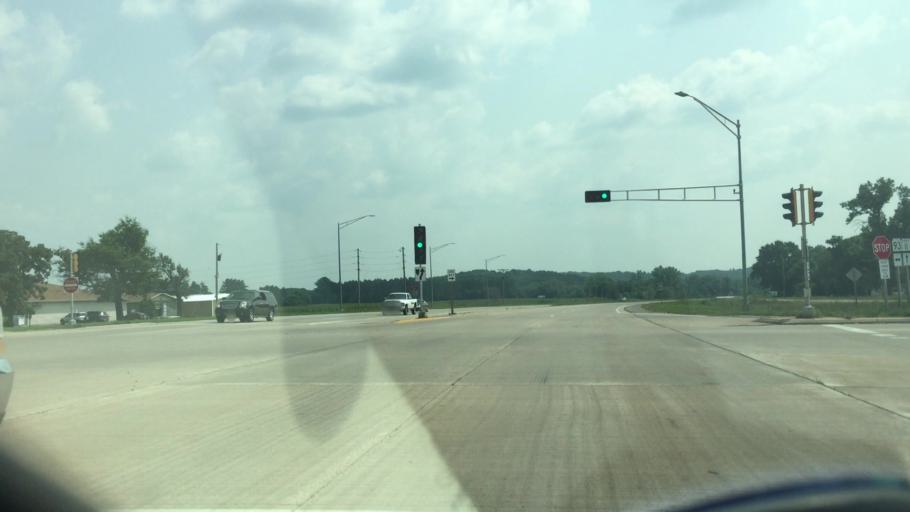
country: US
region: Wisconsin
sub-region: Eau Claire County
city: Altoona
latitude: 44.7417
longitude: -91.4489
